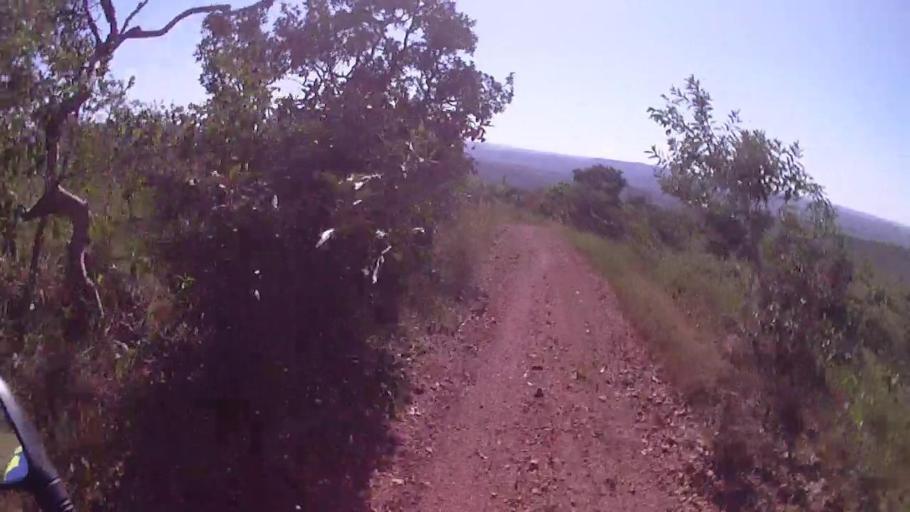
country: BR
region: Federal District
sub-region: Brasilia
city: Brasilia
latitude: -15.8847
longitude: -47.7429
